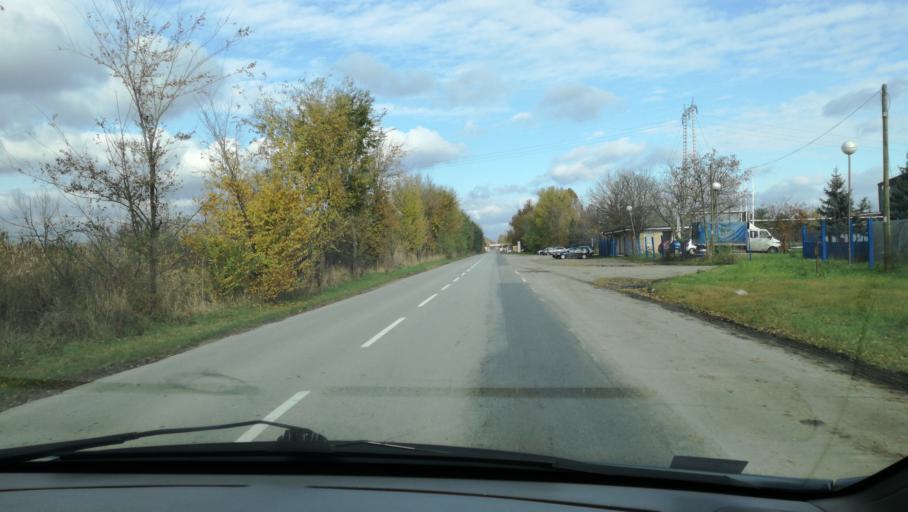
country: RS
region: Autonomna Pokrajina Vojvodina
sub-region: Severnobanatski Okrug
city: Kikinda
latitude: 45.8016
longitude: 20.4420
